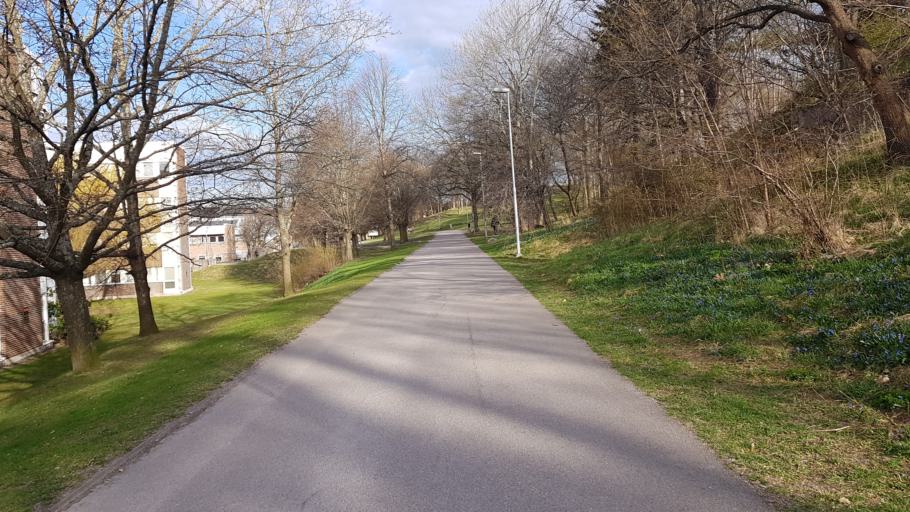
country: SE
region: OEstergoetland
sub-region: Norrkopings Kommun
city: Norrkoping
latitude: 58.5878
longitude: 16.2064
